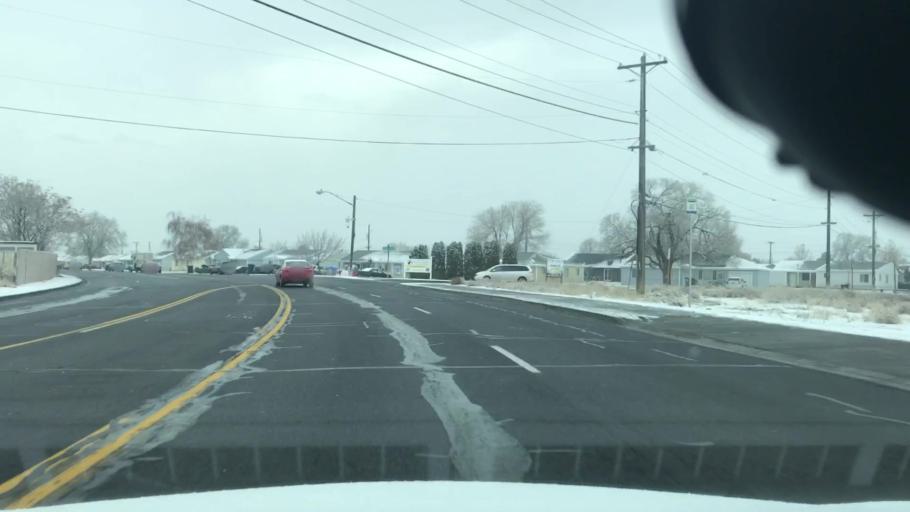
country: US
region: Washington
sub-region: Grant County
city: Moses Lake North
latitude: 47.1788
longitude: -119.3227
